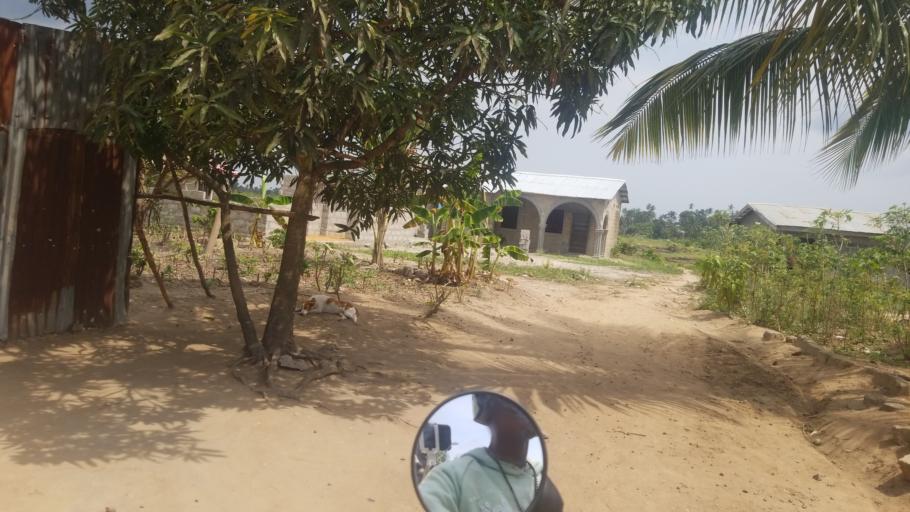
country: SL
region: Western Area
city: Waterloo
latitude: 8.3125
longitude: -13.0486
